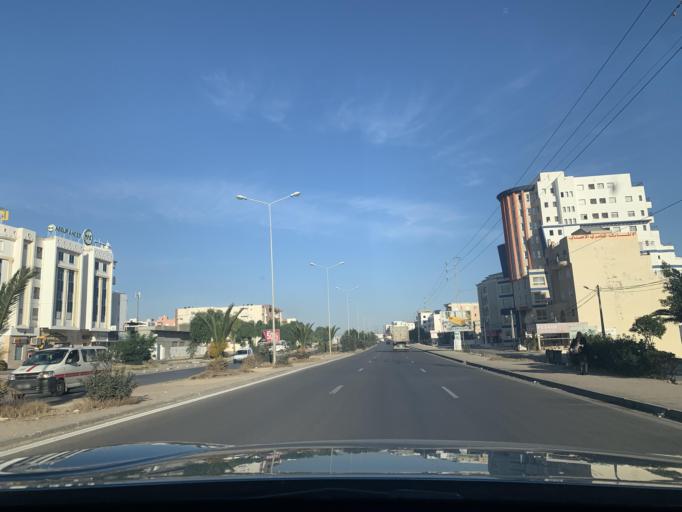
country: DZ
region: Souk Ahras
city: Souk Ahras
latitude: 36.3722
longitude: 7.9957
